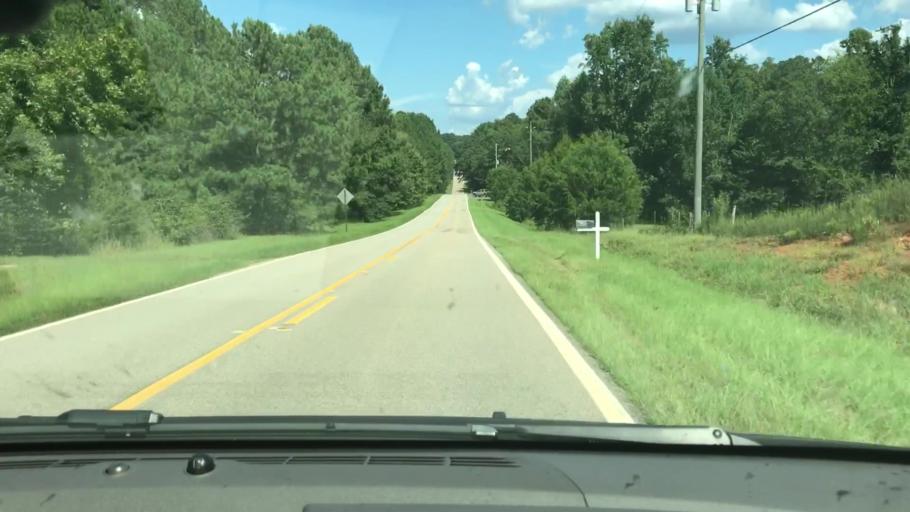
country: US
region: Georgia
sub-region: Troup County
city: La Grange
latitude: 33.1409
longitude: -85.1020
